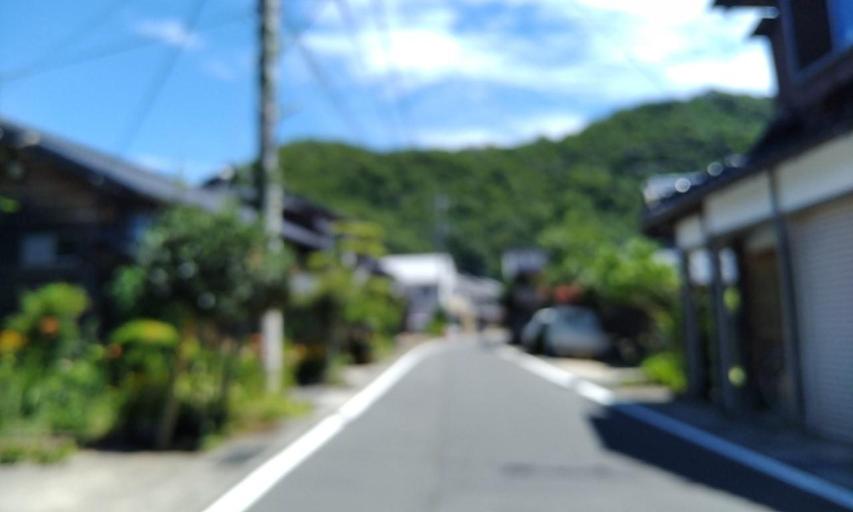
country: JP
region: Kyoto
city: Miyazu
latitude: 35.6670
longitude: 135.2675
